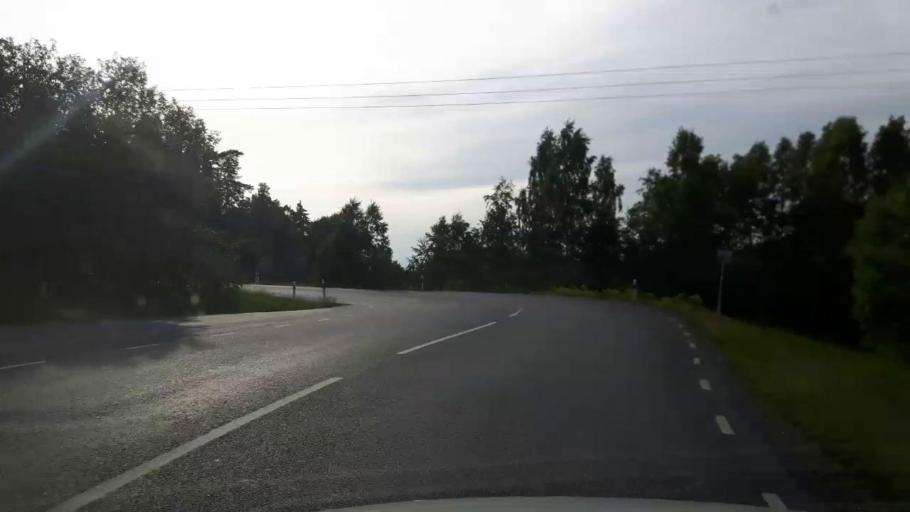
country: SE
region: Uppsala
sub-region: Habo Kommun
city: Balsta
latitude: 59.6255
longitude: 17.4938
